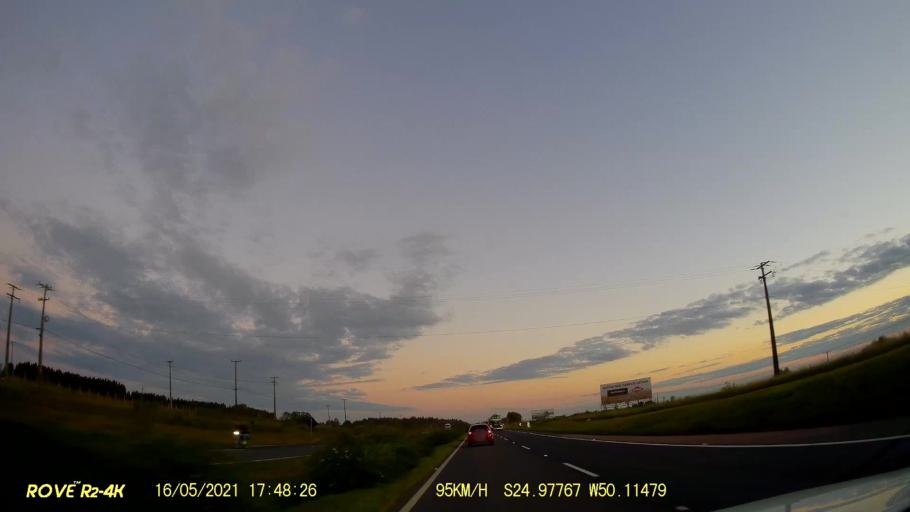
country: BR
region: Parana
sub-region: Carambei
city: Carambei
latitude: -24.9743
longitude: -50.1146
